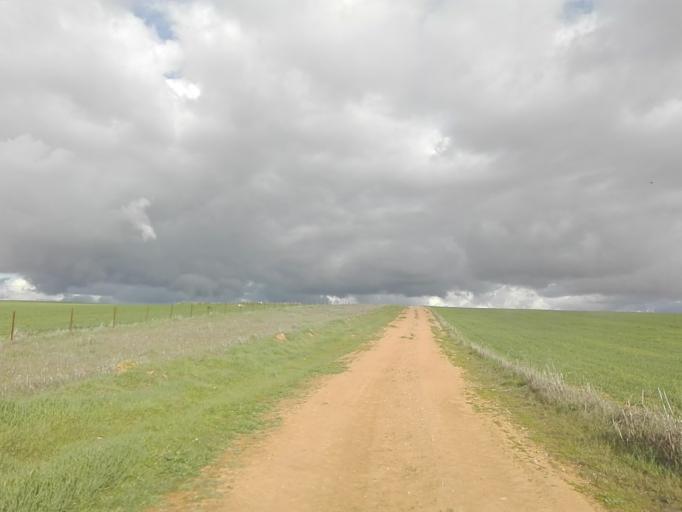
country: ES
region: Extremadura
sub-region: Provincia de Badajoz
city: Llerena
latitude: 38.2850
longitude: -6.0165
